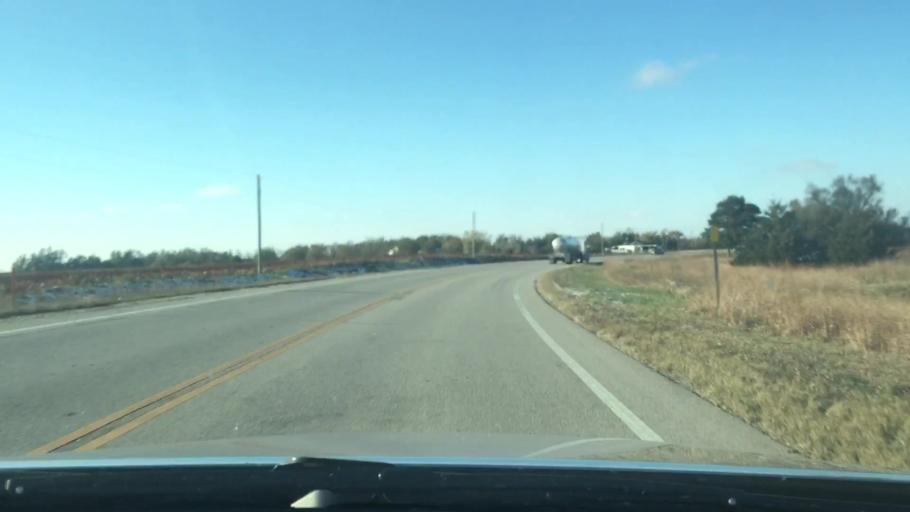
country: US
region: Kansas
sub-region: Rice County
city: Sterling
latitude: 38.1456
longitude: -98.2018
